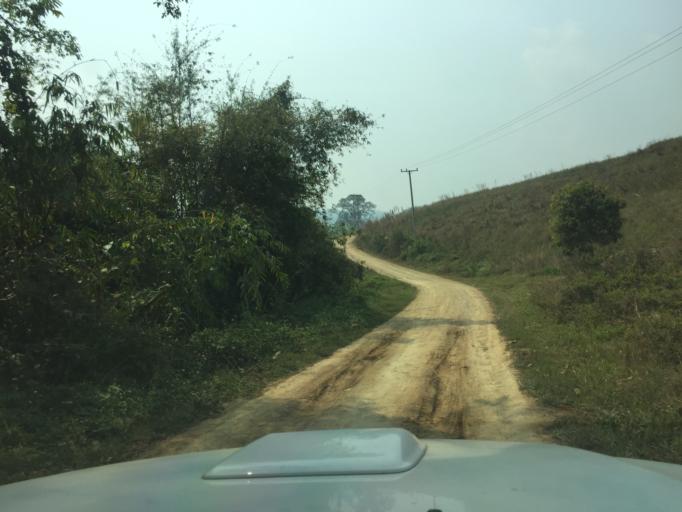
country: TH
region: Phayao
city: Phu Sang
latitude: 19.5875
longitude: 100.5255
